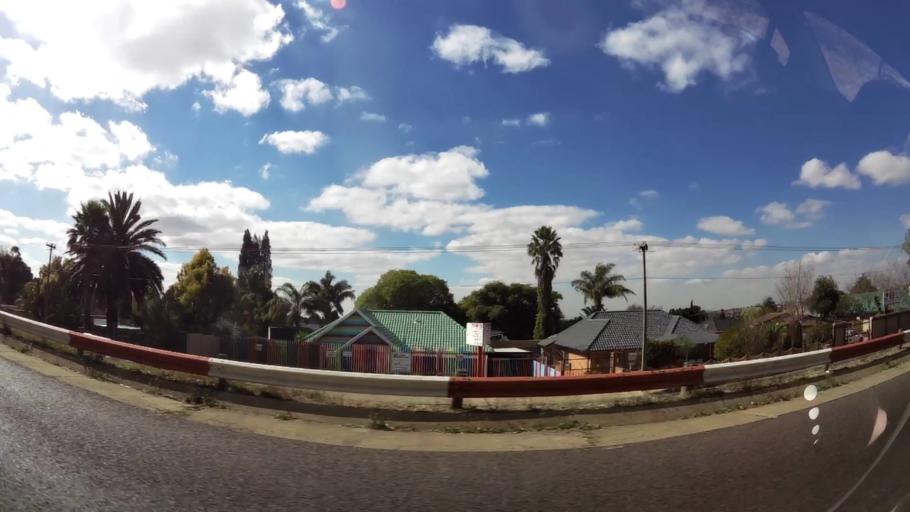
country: ZA
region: Gauteng
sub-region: West Rand District Municipality
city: Krugersdorp
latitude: -26.1158
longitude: 27.8166
